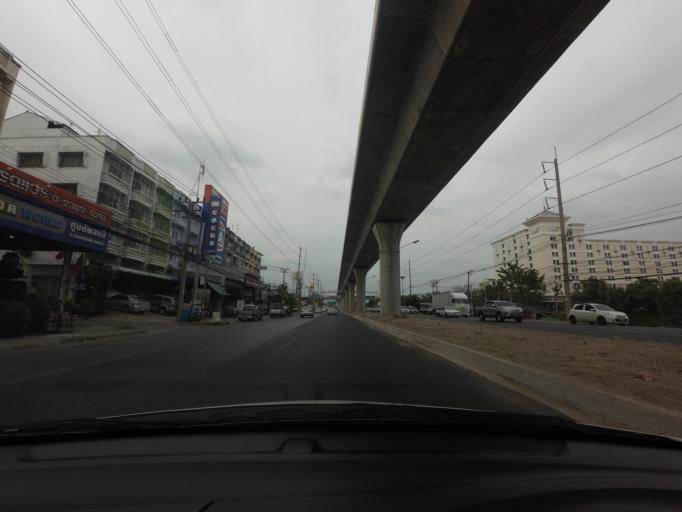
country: TH
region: Samut Prakan
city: Samut Prakan
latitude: 13.5695
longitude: 100.6068
